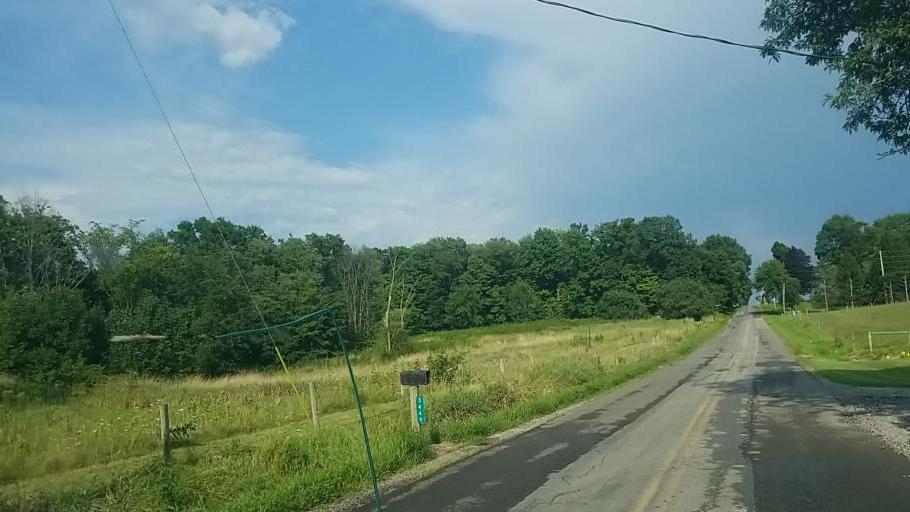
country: US
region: Ohio
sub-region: Wayne County
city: Smithville
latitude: 40.9159
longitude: -81.9000
